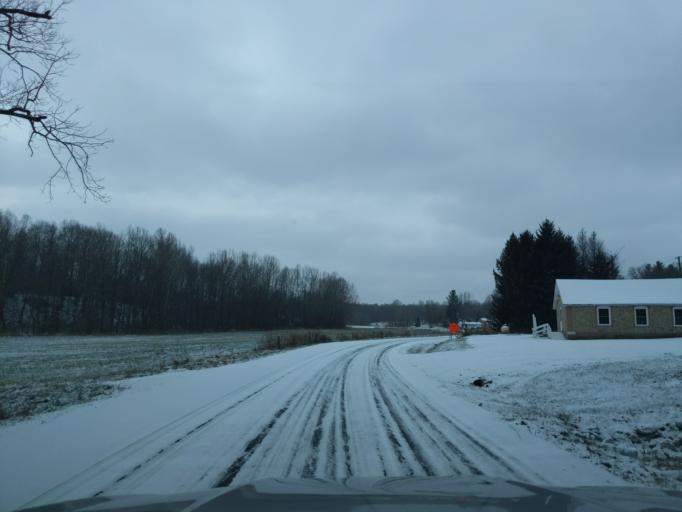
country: US
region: Indiana
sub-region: Decatur County
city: Westport
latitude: 39.2086
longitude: -85.5213
